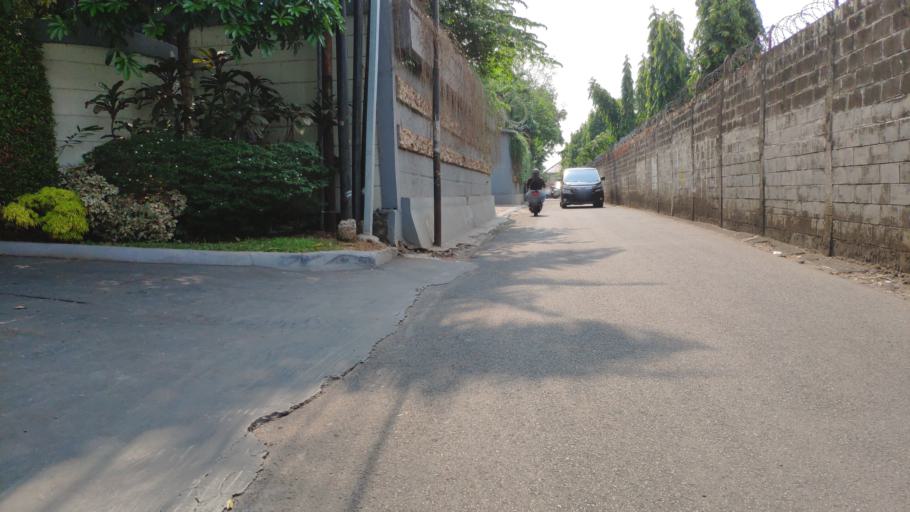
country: ID
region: Jakarta Raya
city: Jakarta
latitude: -6.2658
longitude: 106.8230
